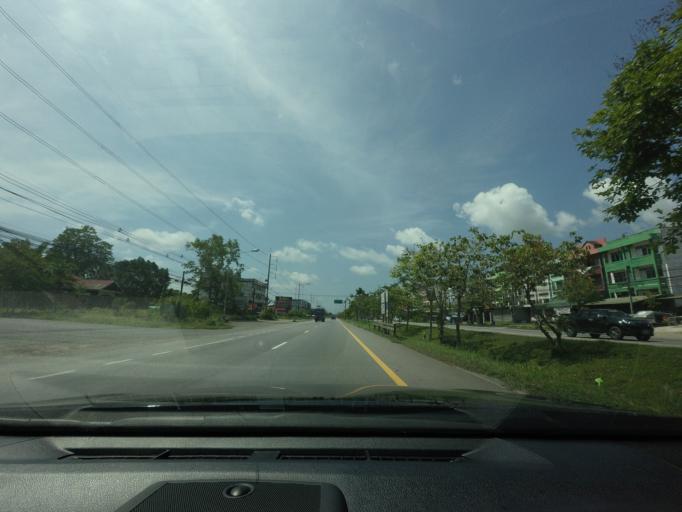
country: TH
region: Chumphon
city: Chumphon
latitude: 10.4877
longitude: 99.1231
